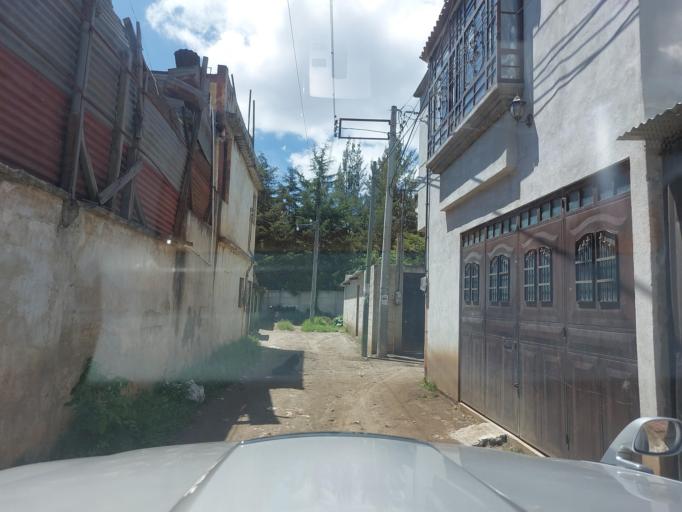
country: GT
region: Chimaltenango
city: El Tejar
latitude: 14.6410
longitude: -90.8117
